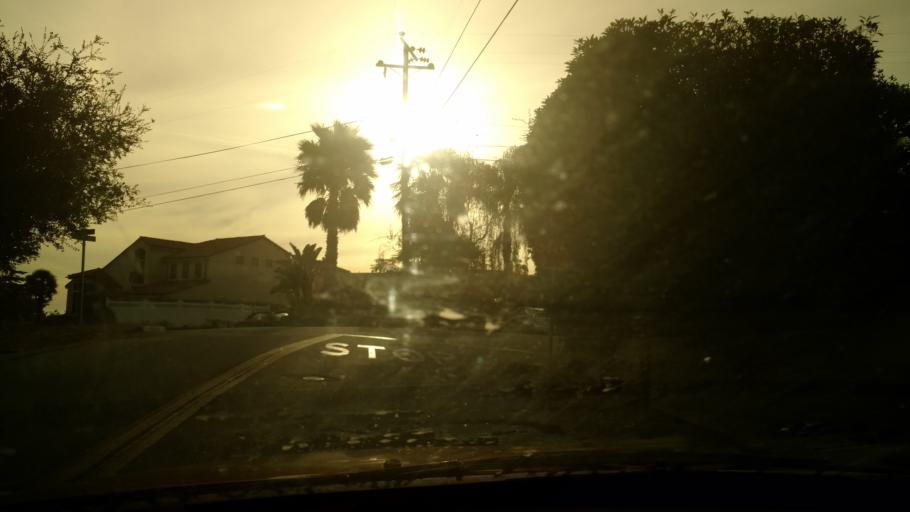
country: US
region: California
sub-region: Santa Cruz County
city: Rio Del Mar
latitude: 36.9669
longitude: -121.8777
